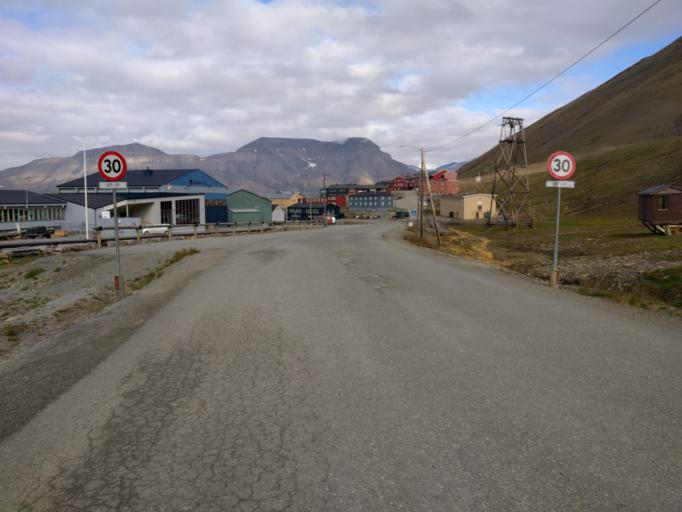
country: SJ
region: Svalbard
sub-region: Spitsbergen
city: Longyearbyen
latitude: 78.2093
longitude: 15.6114
